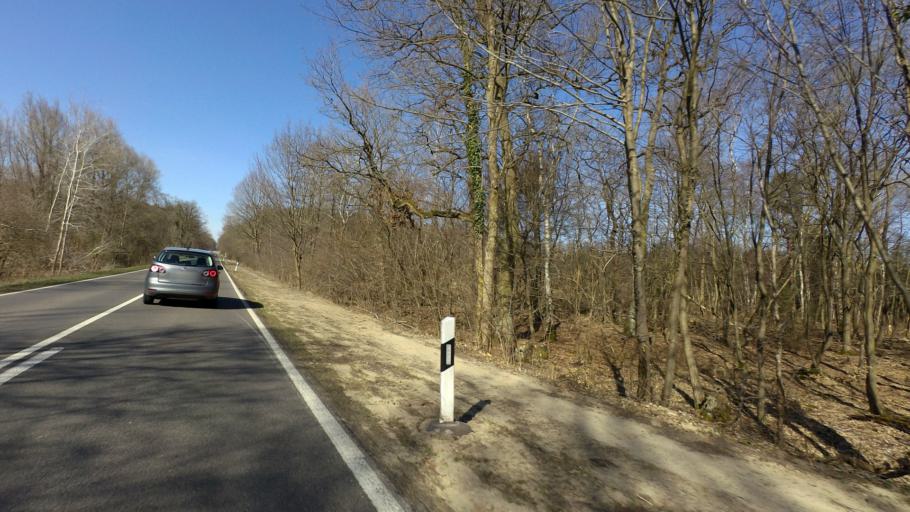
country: DE
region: Brandenburg
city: Eberswalde
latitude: 52.8142
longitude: 13.8334
